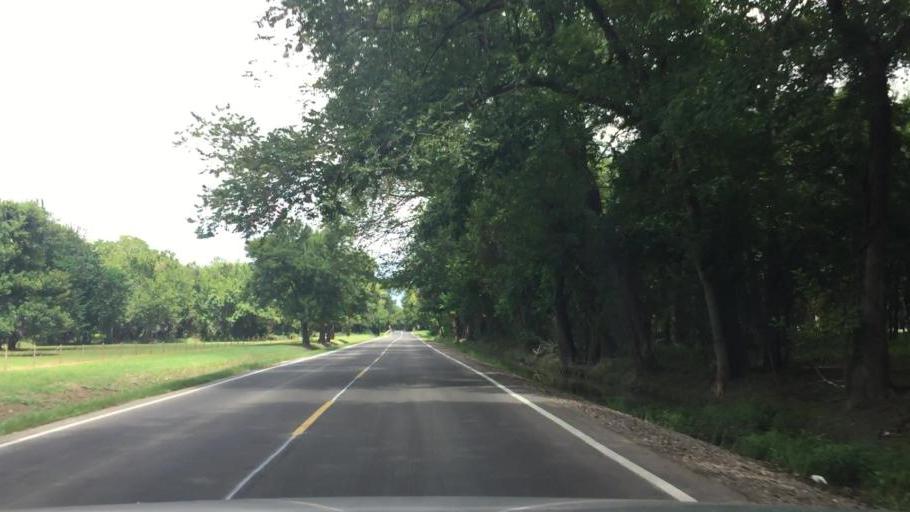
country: US
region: Texas
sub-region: Harris County
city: Jersey Village
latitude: 29.8133
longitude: -95.6366
